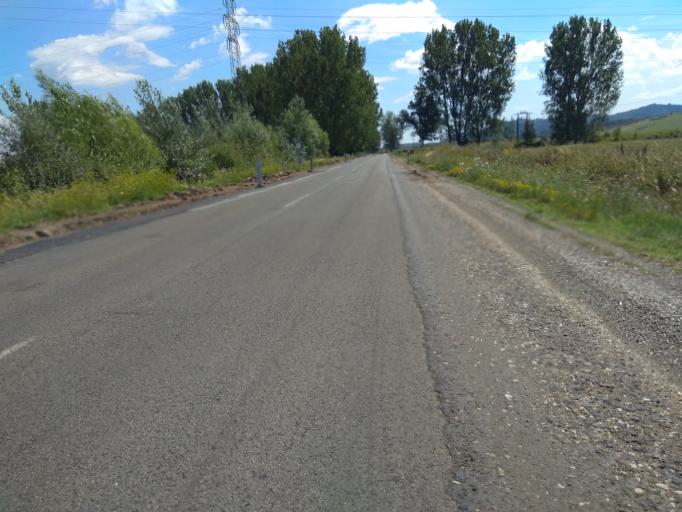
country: HU
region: Borsod-Abauj-Zemplen
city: Sajokaza
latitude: 48.2679
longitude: 20.5950
